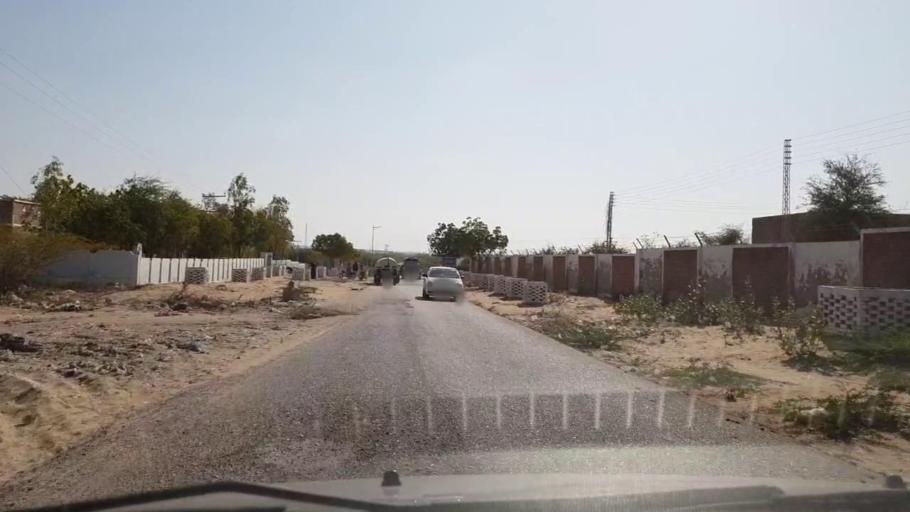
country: PK
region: Sindh
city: Diplo
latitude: 24.4774
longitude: 69.5806
